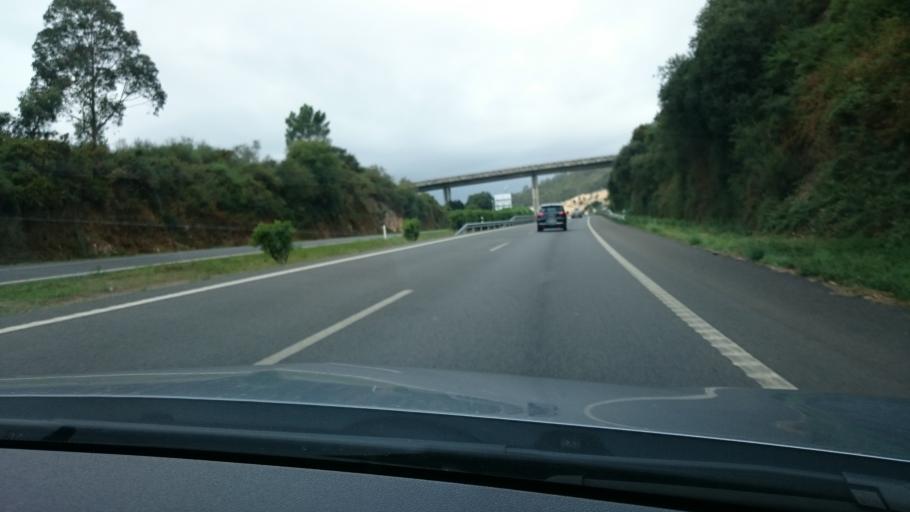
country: ES
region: Galicia
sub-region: Provincia da Coruna
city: Culleredo
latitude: 43.2783
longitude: -8.4183
